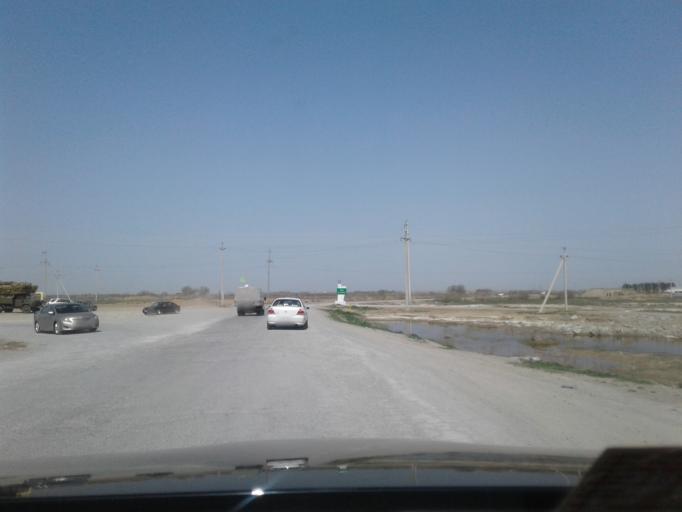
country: TM
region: Ahal
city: Abadan
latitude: 38.1768
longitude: 57.9813
